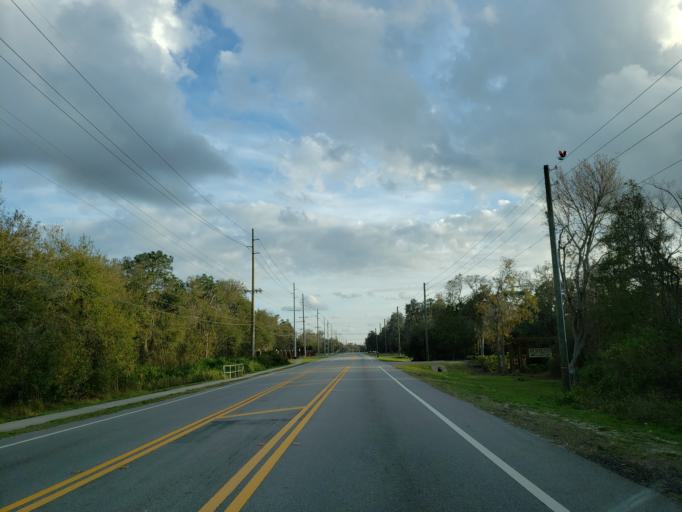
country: US
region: Florida
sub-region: Hillsborough County
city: Riverview
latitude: 27.8397
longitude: -82.3020
